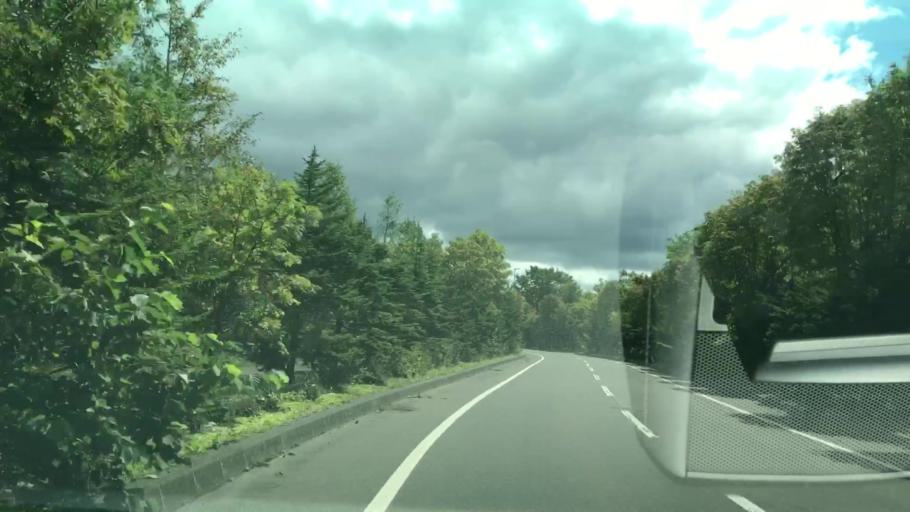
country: JP
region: Hokkaido
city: Chitose
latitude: 42.7786
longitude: 141.6036
